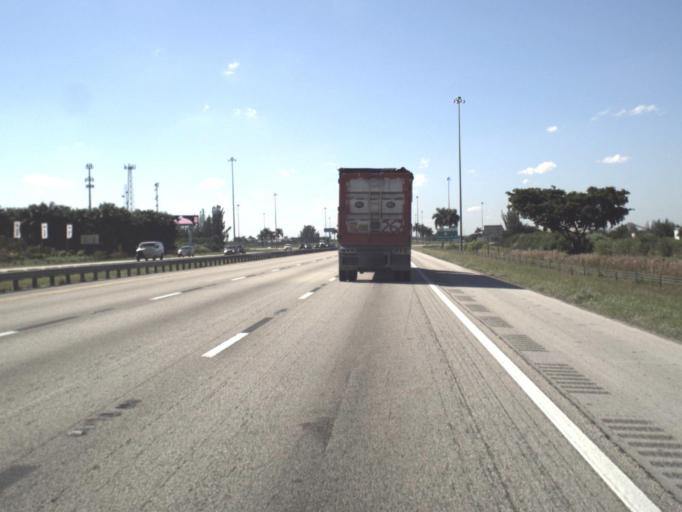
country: US
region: Florida
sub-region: Miami-Dade County
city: Palm Springs North
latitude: 25.9106
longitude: -80.3819
